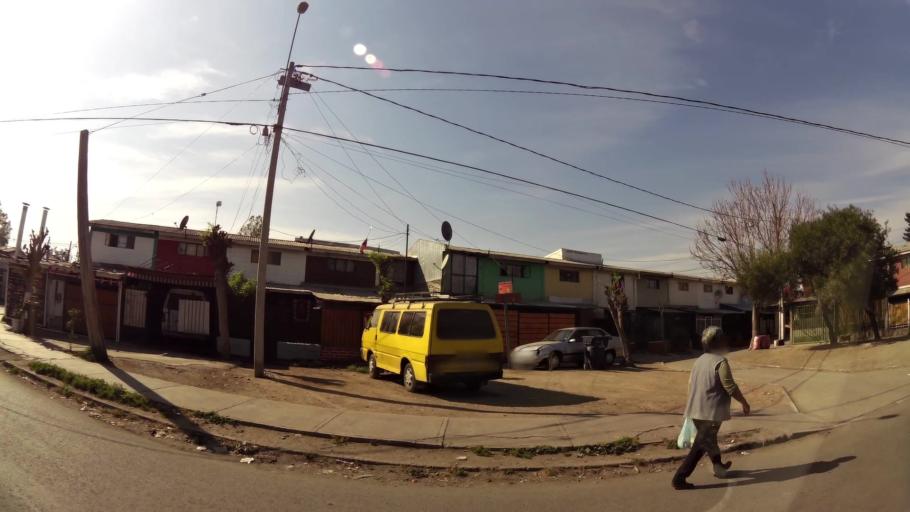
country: CL
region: Santiago Metropolitan
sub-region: Provincia de Santiago
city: La Pintana
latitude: -33.5629
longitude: -70.6391
